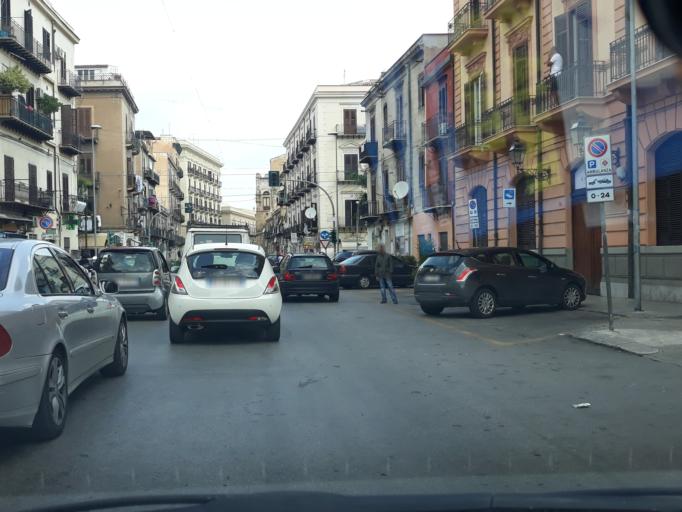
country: IT
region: Sicily
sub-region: Palermo
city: Palermo
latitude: 38.1111
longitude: 13.3688
